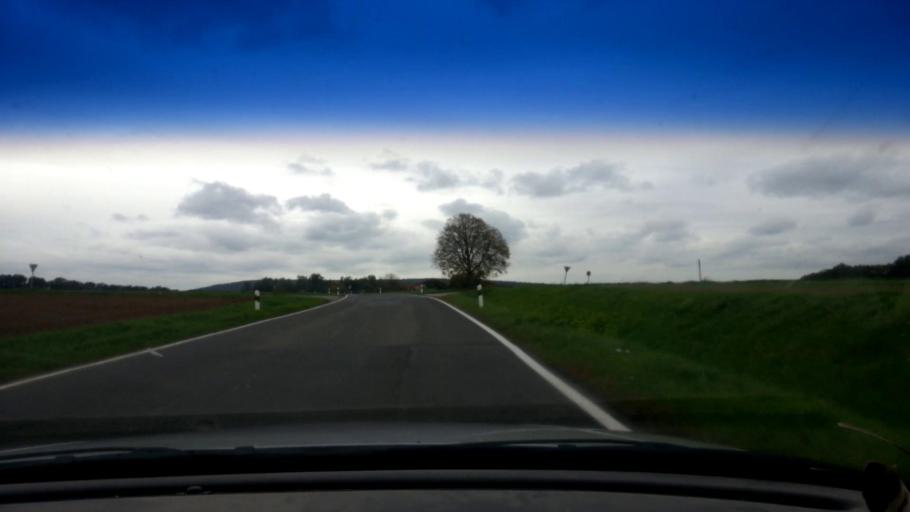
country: DE
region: Bavaria
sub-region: Upper Franconia
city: Gerach
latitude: 50.0254
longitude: 10.8162
